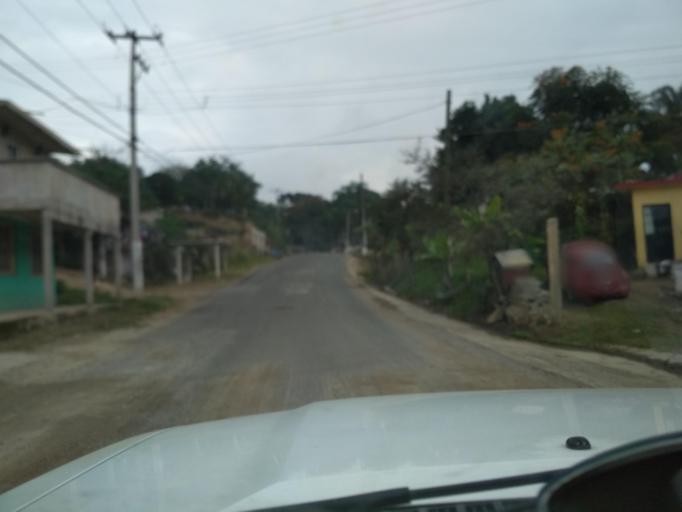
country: MX
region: Veracruz
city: El Castillo
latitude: 19.5636
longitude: -96.8623
